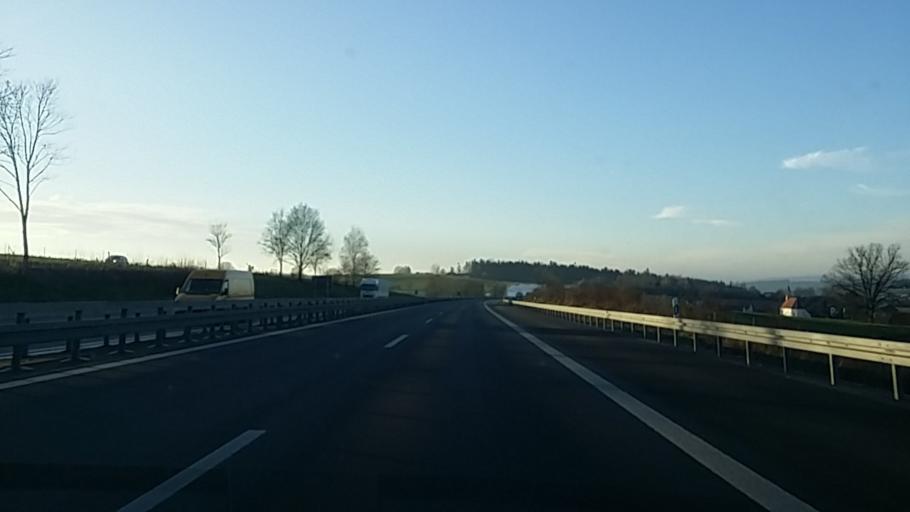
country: DE
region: Bavaria
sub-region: Lower Bavaria
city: Niederwinkling
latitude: 48.9035
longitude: 12.7851
